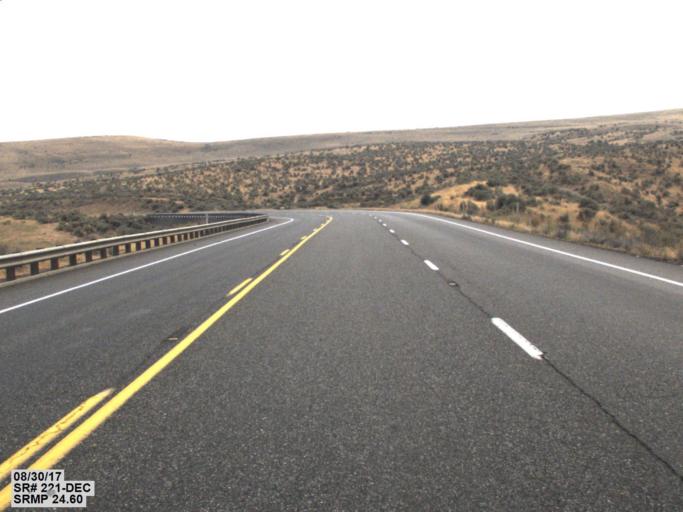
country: US
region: Washington
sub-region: Benton County
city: Prosser
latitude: 46.2032
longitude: -119.7238
